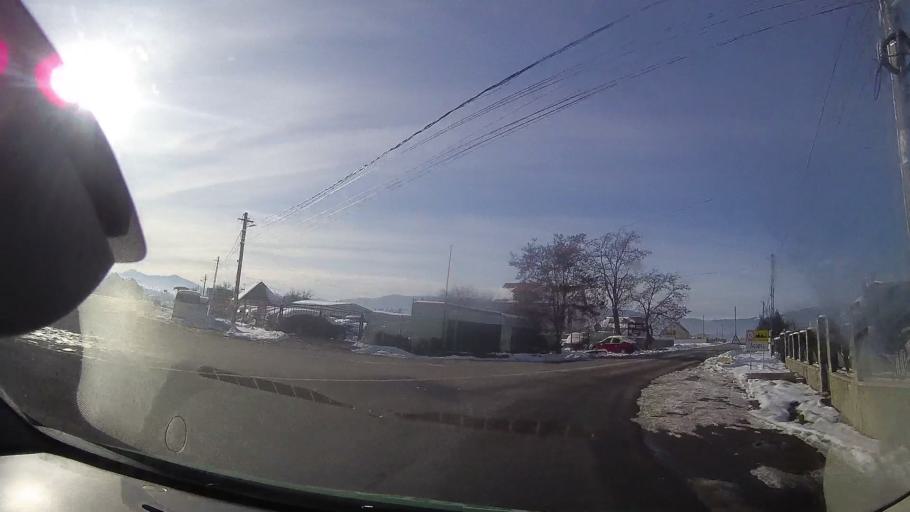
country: RO
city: Vanatori-Neamt
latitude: 47.1730
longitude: 26.3247
